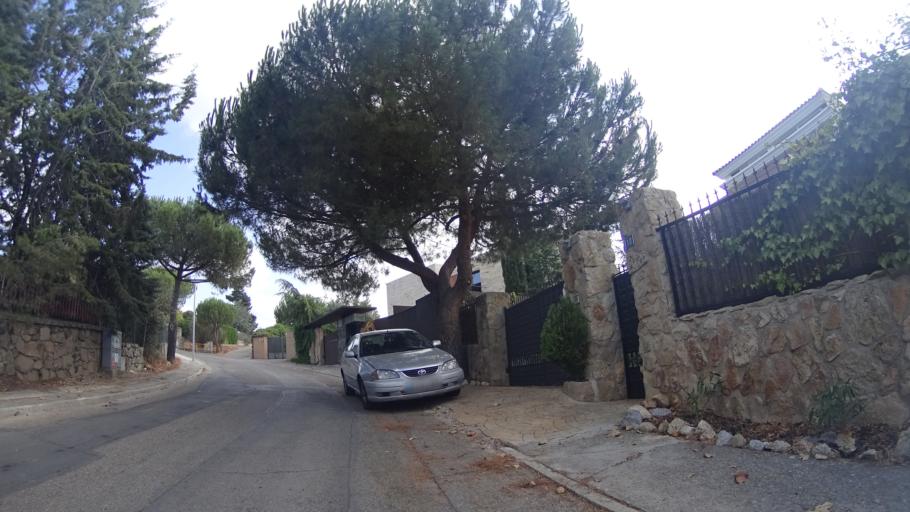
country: ES
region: Madrid
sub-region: Provincia de Madrid
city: Torrelodones
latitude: 40.5872
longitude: -3.9174
